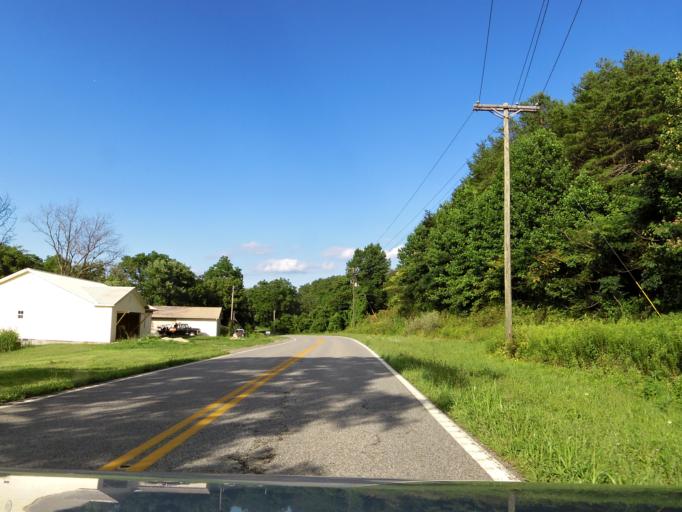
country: US
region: Tennessee
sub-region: Blount County
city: Maryville
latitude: 35.6227
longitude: -84.0274
